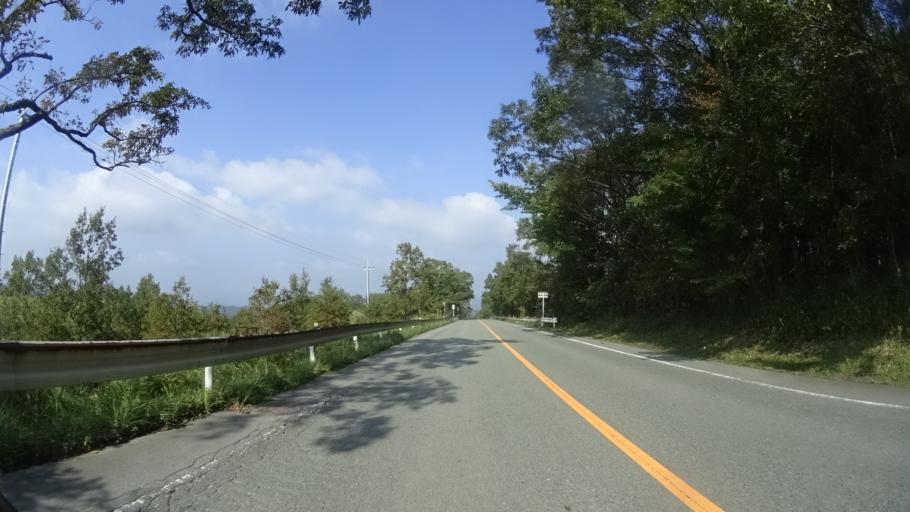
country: JP
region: Kumamoto
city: Aso
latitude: 33.0352
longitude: 131.0660
